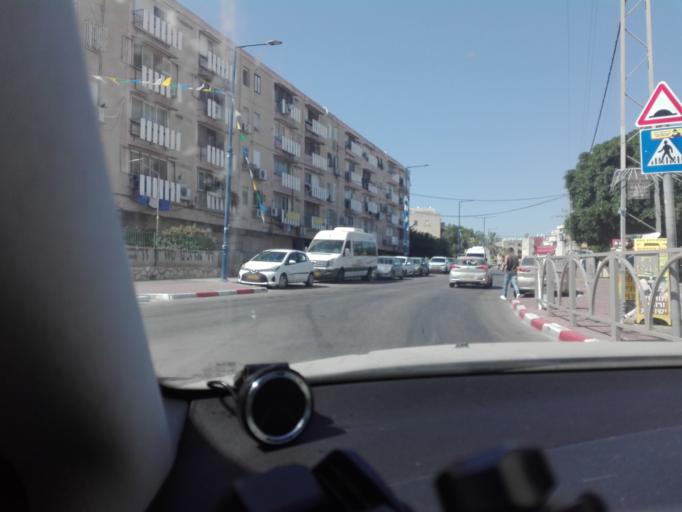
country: IL
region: Central District
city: Bene 'Ayish
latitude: 31.7296
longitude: 34.7387
